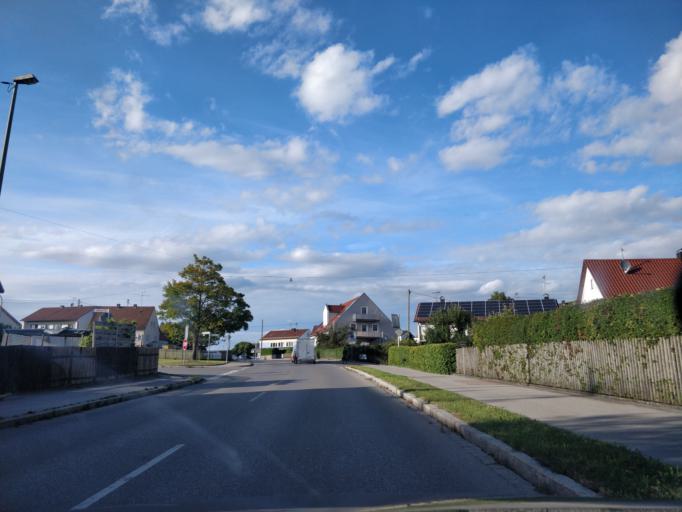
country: DE
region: Bavaria
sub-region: Swabia
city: Friedberg
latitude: 48.3374
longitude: 11.0022
